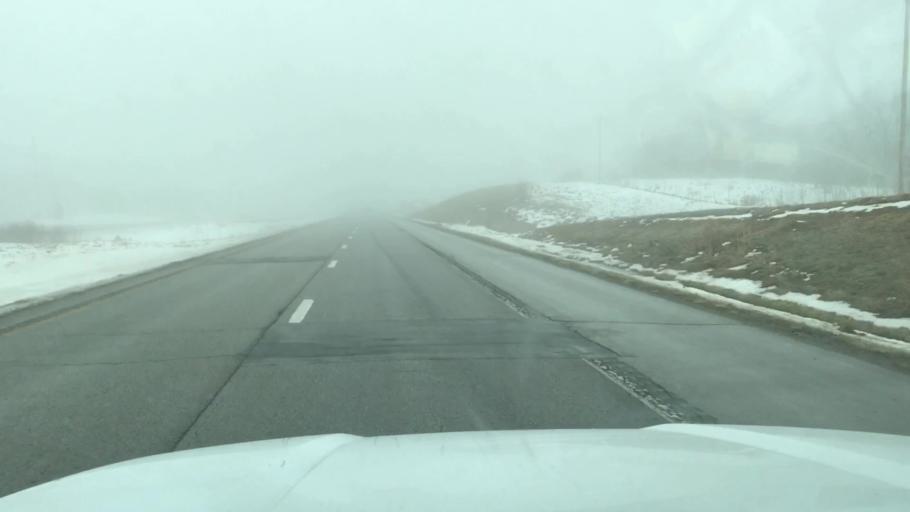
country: US
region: Missouri
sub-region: Clinton County
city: Cameron
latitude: 39.7550
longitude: -94.3095
